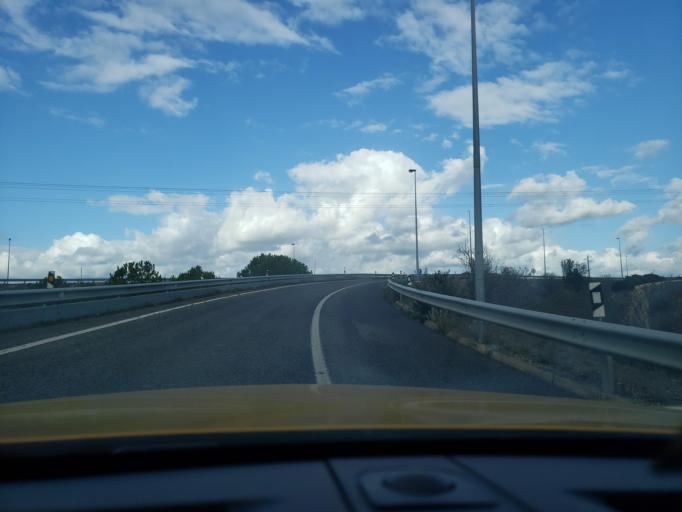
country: PT
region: Faro
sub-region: Portimao
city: Portimao
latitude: 37.1752
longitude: -8.5673
